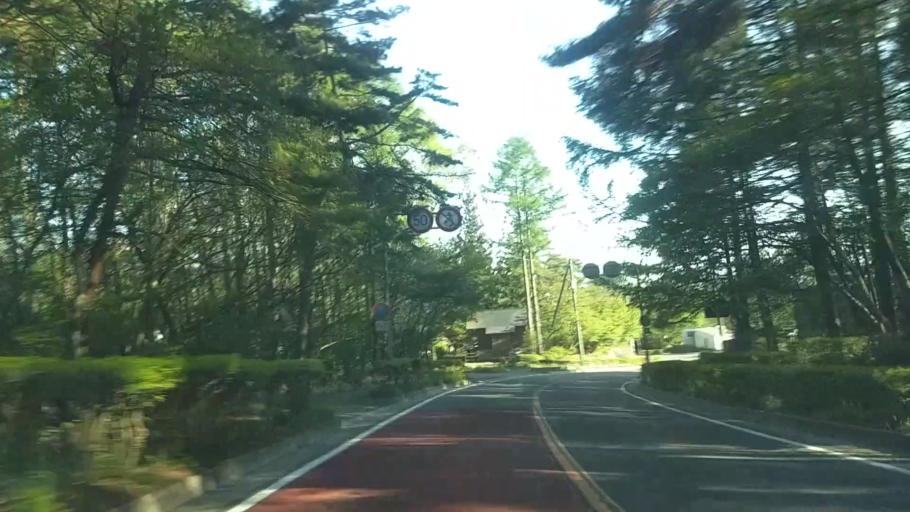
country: JP
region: Yamanashi
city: Nirasaki
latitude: 35.9204
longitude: 138.4352
